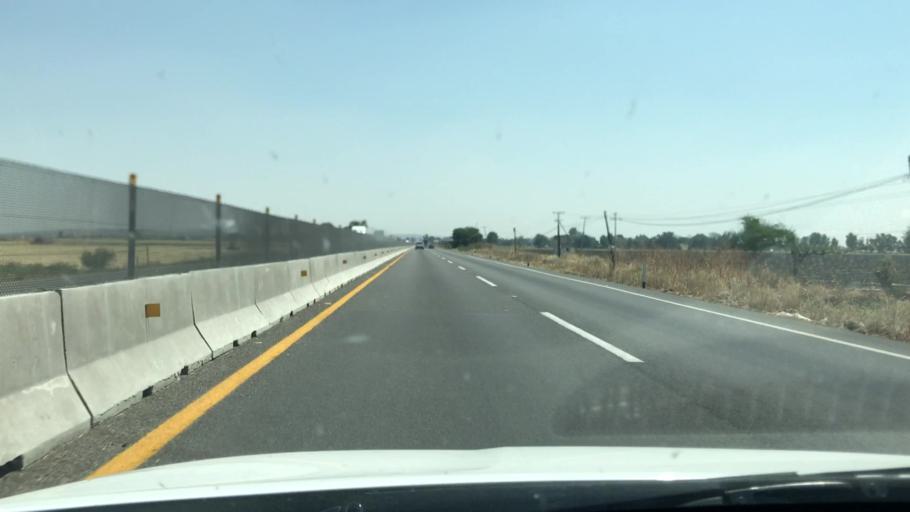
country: MX
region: Guanajuato
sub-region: Abasolo
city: San Bernardo Pena Blanca
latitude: 20.4780
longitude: -101.4980
